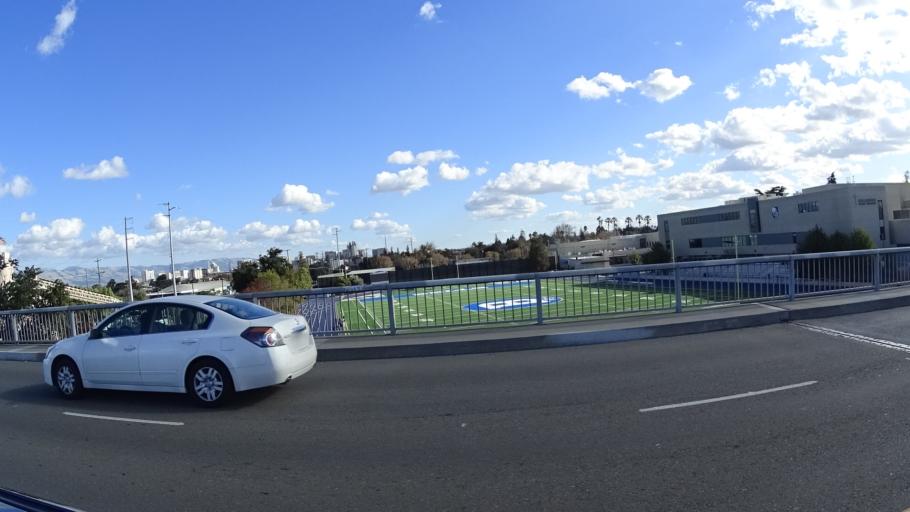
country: US
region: California
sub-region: Santa Clara County
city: Buena Vista
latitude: 37.3440
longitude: -121.9183
